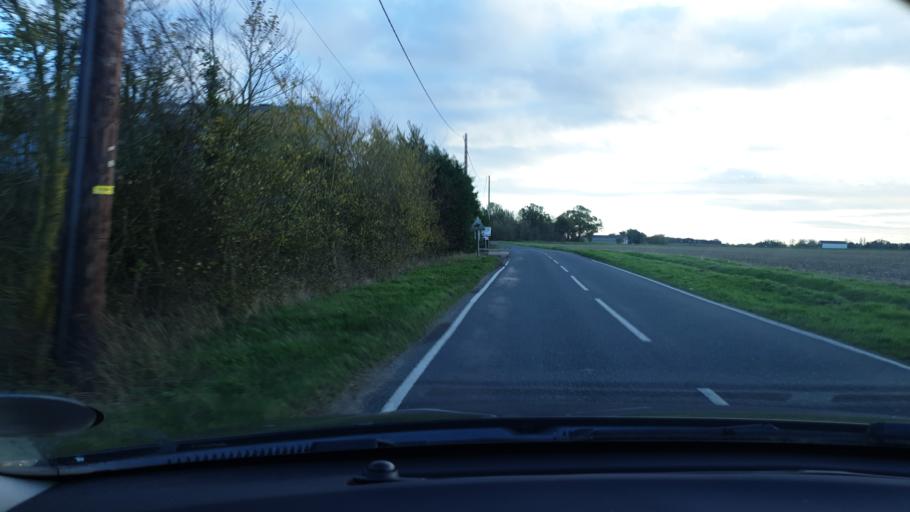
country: GB
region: England
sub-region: Essex
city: Mistley
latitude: 51.9090
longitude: 1.1432
